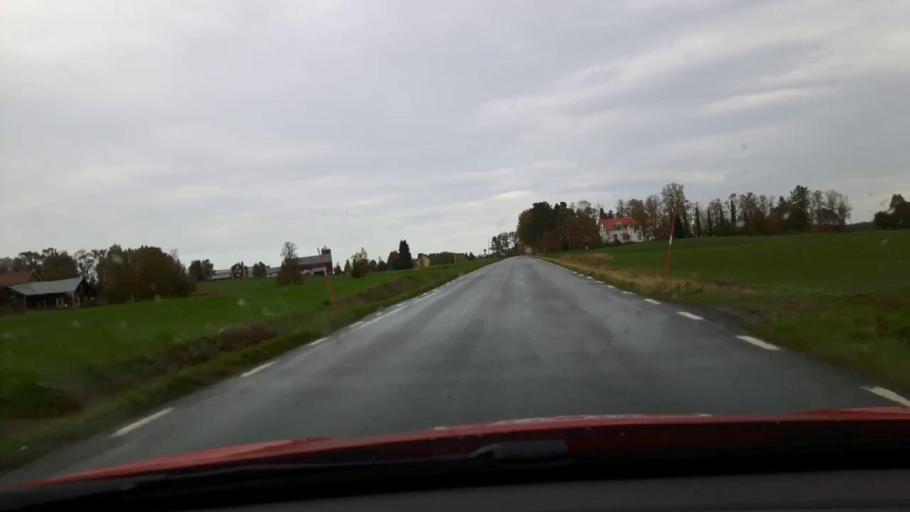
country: SE
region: Jaemtland
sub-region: Bergs Kommun
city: Hoverberg
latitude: 63.0327
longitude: 14.3452
